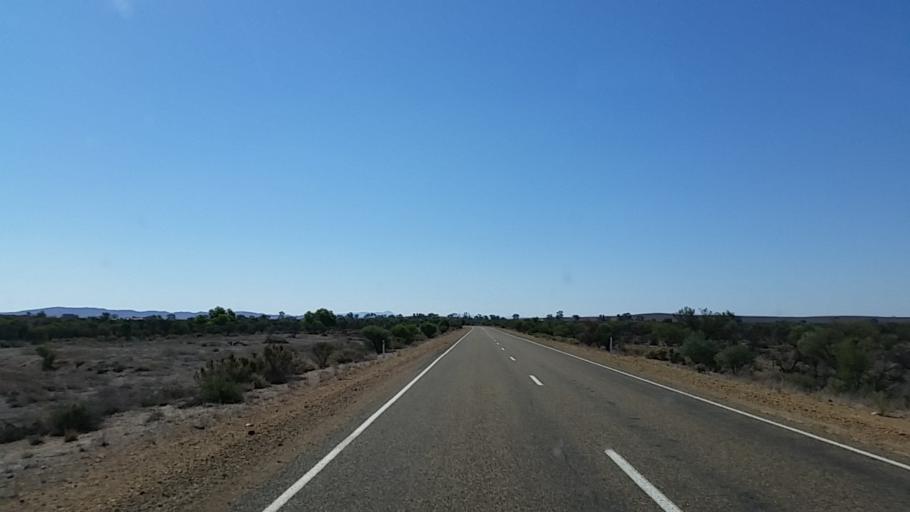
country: AU
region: South Australia
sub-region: Flinders Ranges
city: Quorn
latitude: -32.0844
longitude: 138.5031
